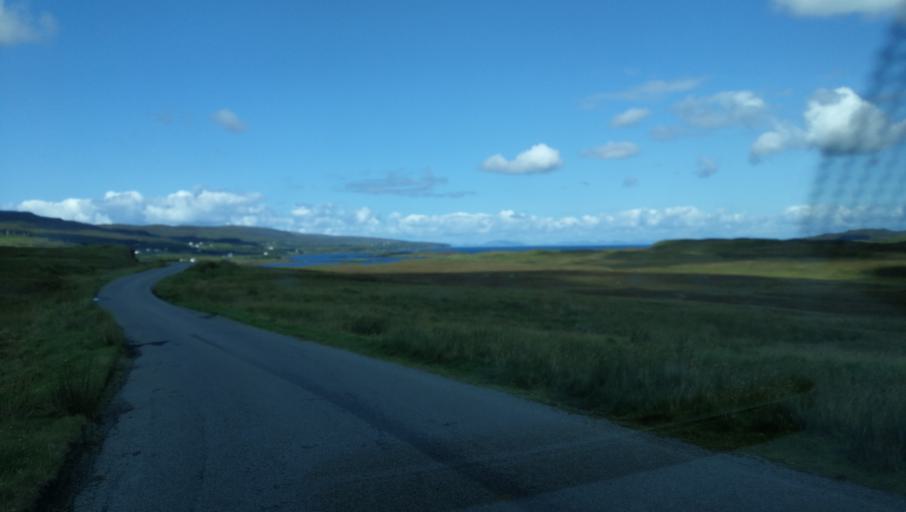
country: GB
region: Scotland
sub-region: Highland
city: Isle of Skye
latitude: 57.4285
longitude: -6.6074
